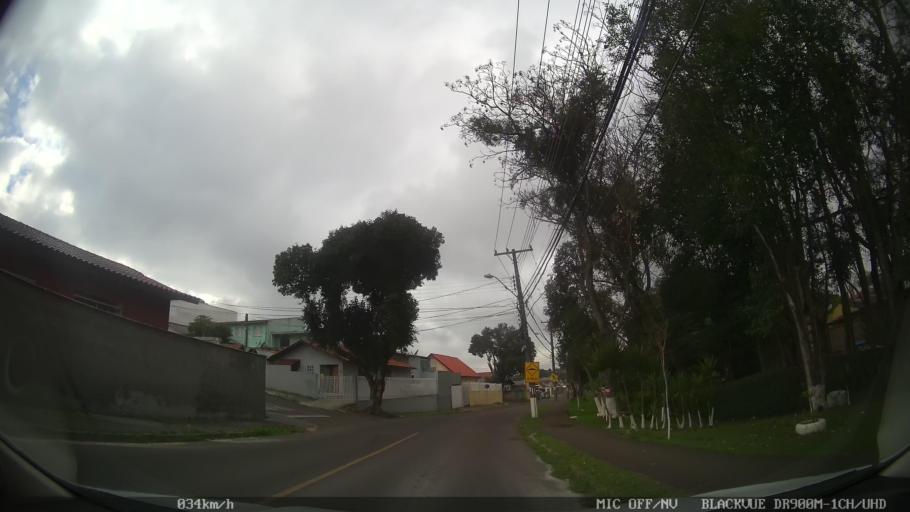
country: BR
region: Parana
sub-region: Curitiba
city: Curitiba
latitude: -25.3786
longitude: -49.2596
